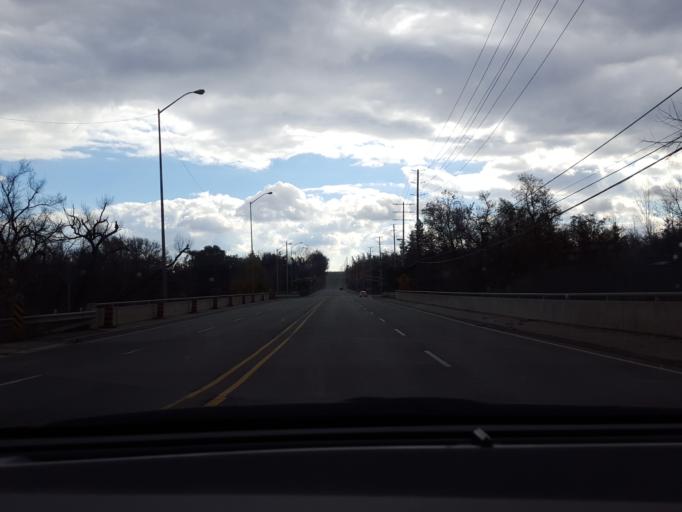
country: CA
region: Ontario
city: Brampton
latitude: 43.6456
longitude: -79.8007
